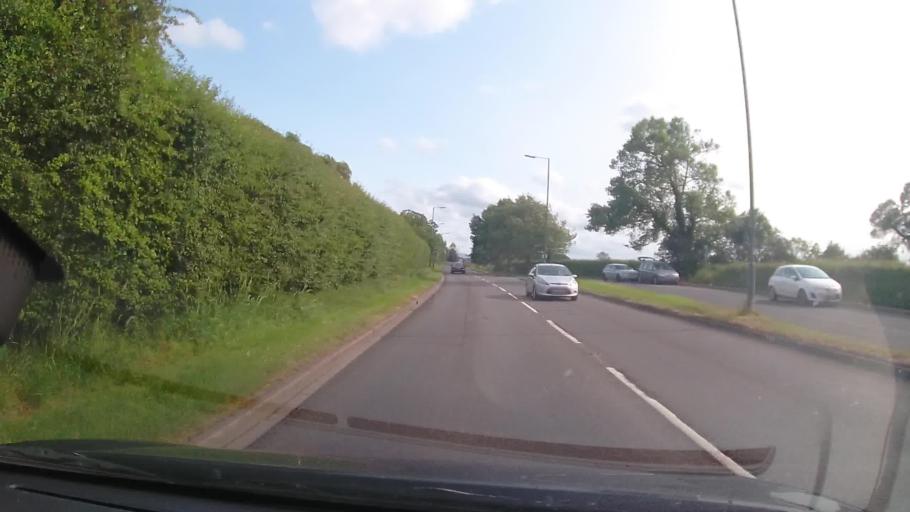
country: GB
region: England
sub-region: Shropshire
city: Shrewsbury
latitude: 52.7396
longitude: -2.7455
